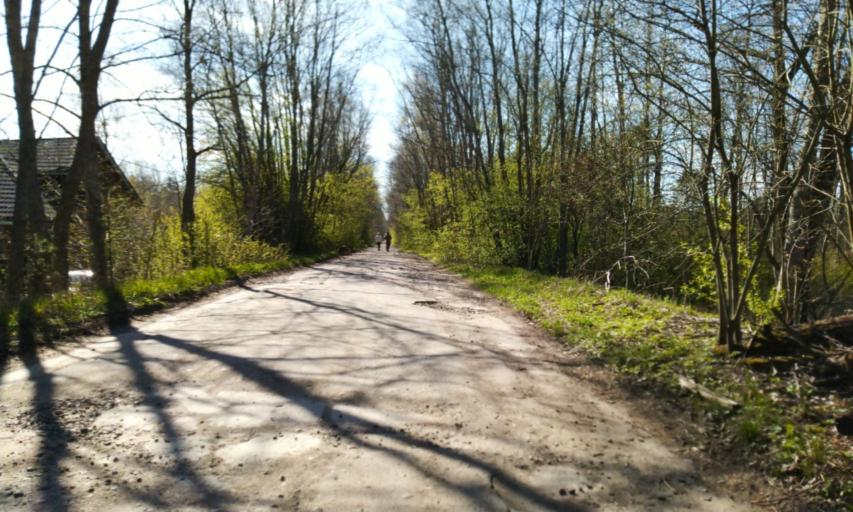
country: RU
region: Leningrad
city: Garbolovo
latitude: 60.3889
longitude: 30.4820
